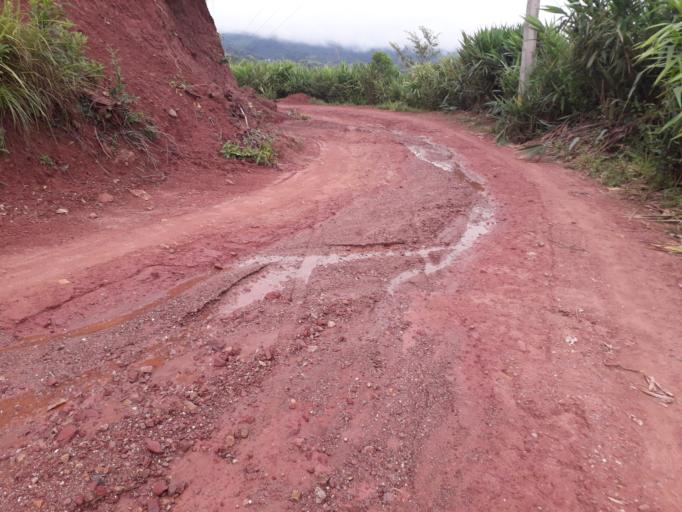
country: CN
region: Yunnan
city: Menglie
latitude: 22.2635
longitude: 101.5815
